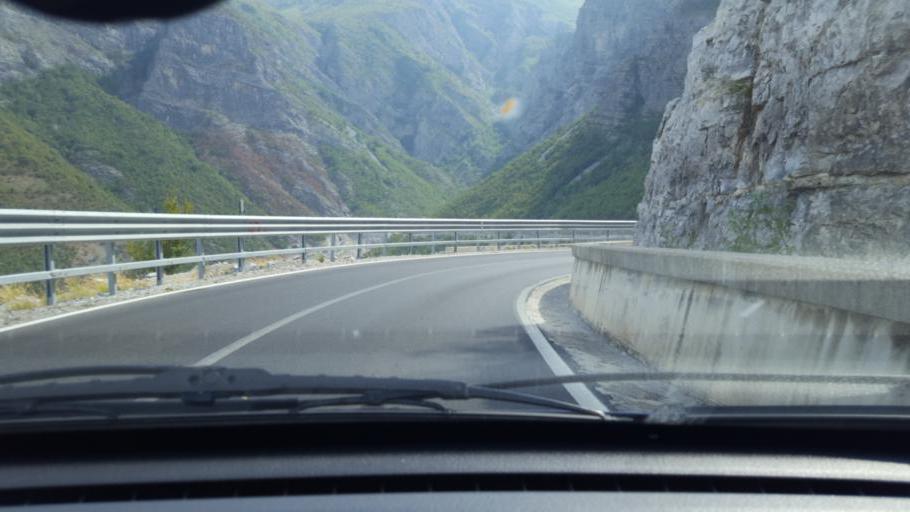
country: AL
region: Shkoder
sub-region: Rrethi i Malesia e Madhe
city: Kastrat
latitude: 42.4207
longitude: 19.5049
